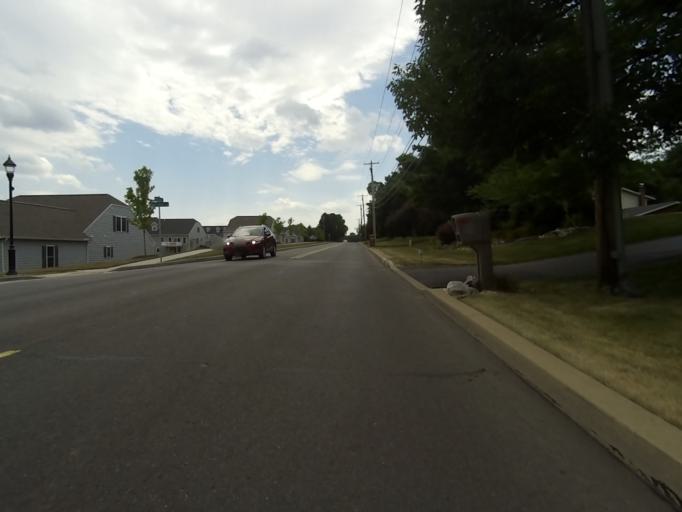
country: US
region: Pennsylvania
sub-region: Centre County
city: Park Forest Village
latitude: 40.7924
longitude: -77.8996
